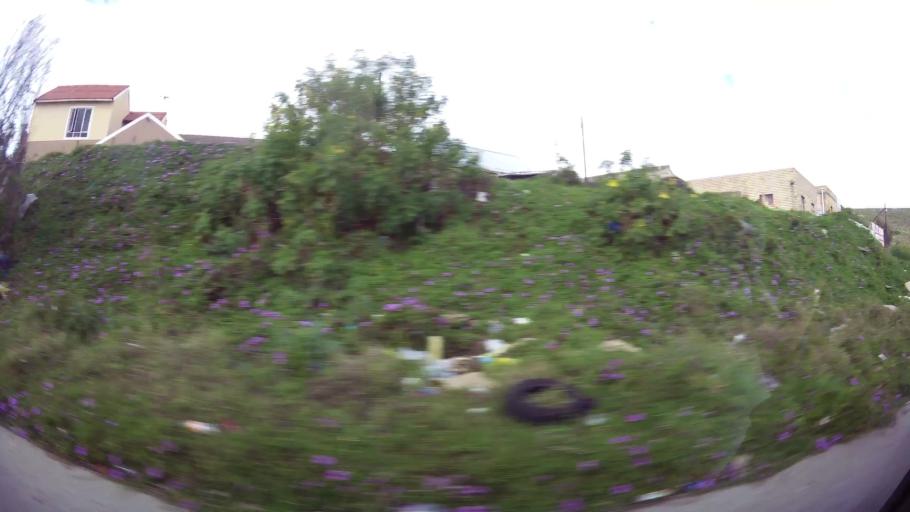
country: ZA
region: Eastern Cape
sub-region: Nelson Mandela Bay Metropolitan Municipality
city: Port Elizabeth
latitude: -33.9268
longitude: 25.5631
